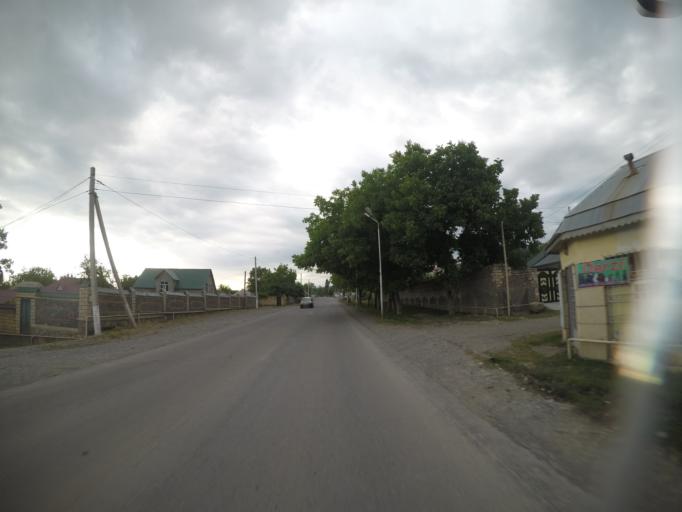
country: AZ
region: Qabala Rayon
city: Qutqashen
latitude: 40.9471
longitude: 47.9409
